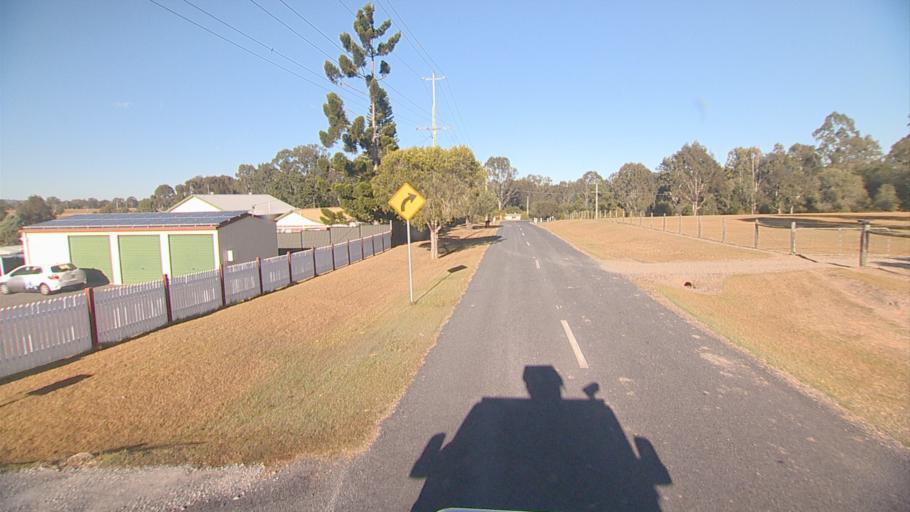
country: AU
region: Queensland
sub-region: Logan
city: North Maclean
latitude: -27.7994
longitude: 153.0054
